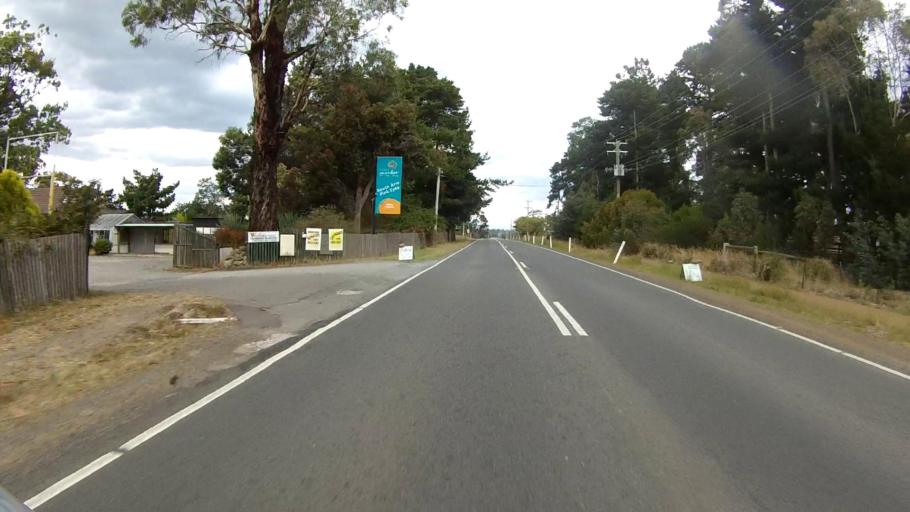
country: AU
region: Tasmania
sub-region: Clarence
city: Cambridge
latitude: -42.8383
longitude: 147.4649
